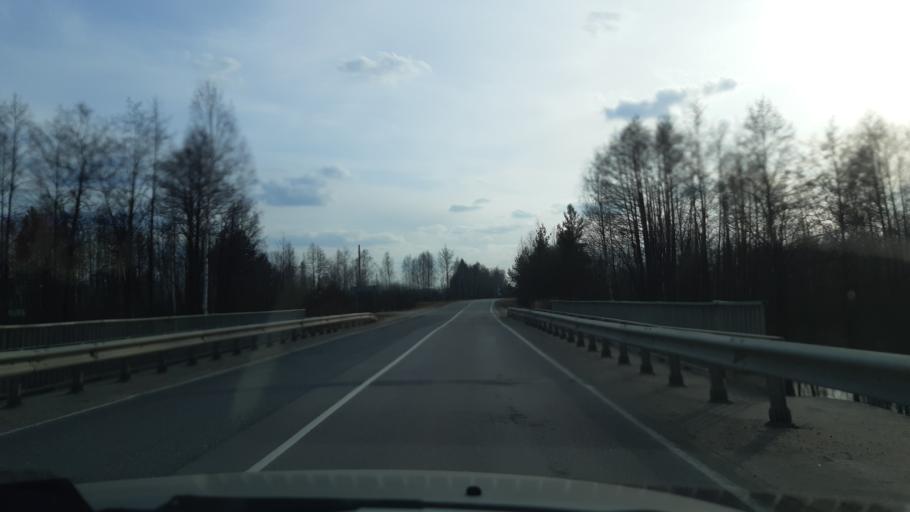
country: RU
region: Vladimir
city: Luknovo
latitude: 56.1789
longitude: 42.0093
